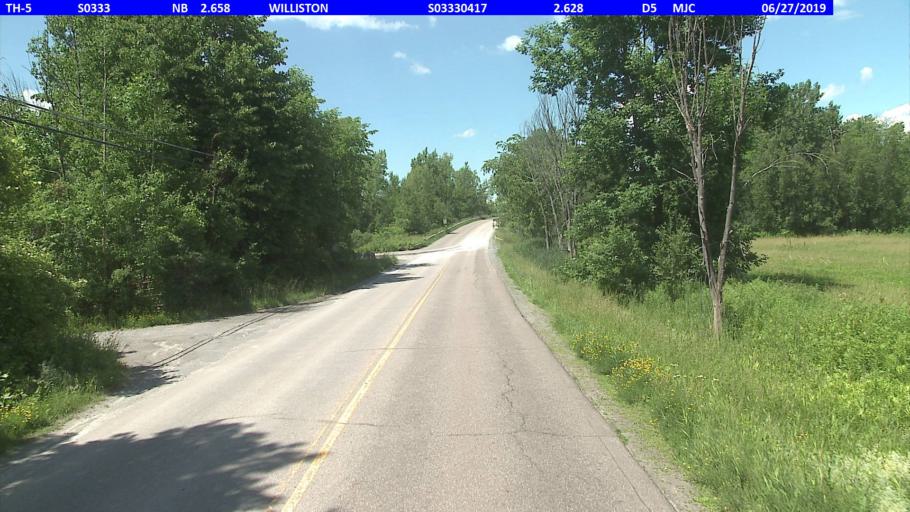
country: US
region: Vermont
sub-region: Chittenden County
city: South Burlington
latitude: 44.4388
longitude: -73.1315
